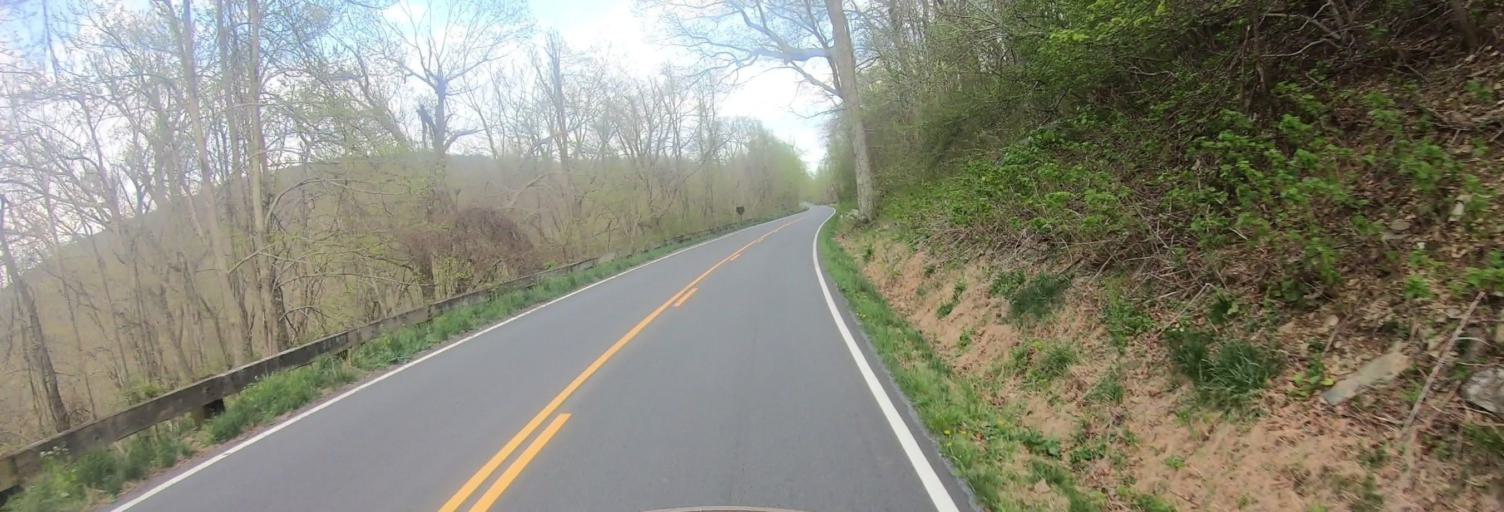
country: US
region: Virginia
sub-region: Augusta County
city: Dooms
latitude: 38.0614
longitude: -78.8206
